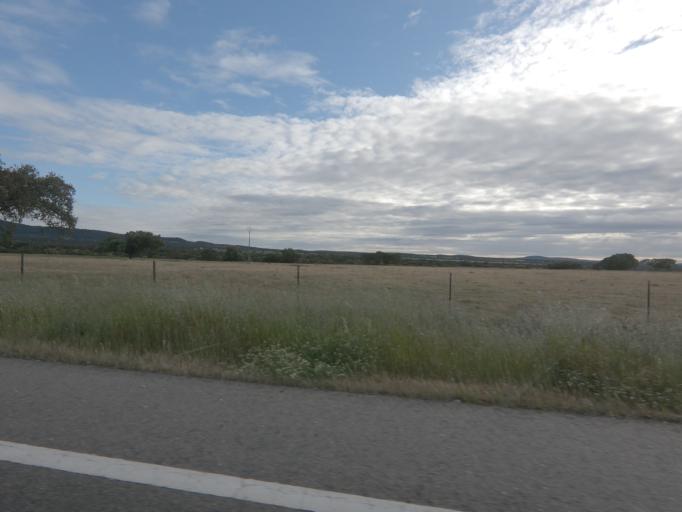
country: ES
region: Extremadura
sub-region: Provincia de Caceres
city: Torrejoncillo
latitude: 39.8671
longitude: -6.4366
